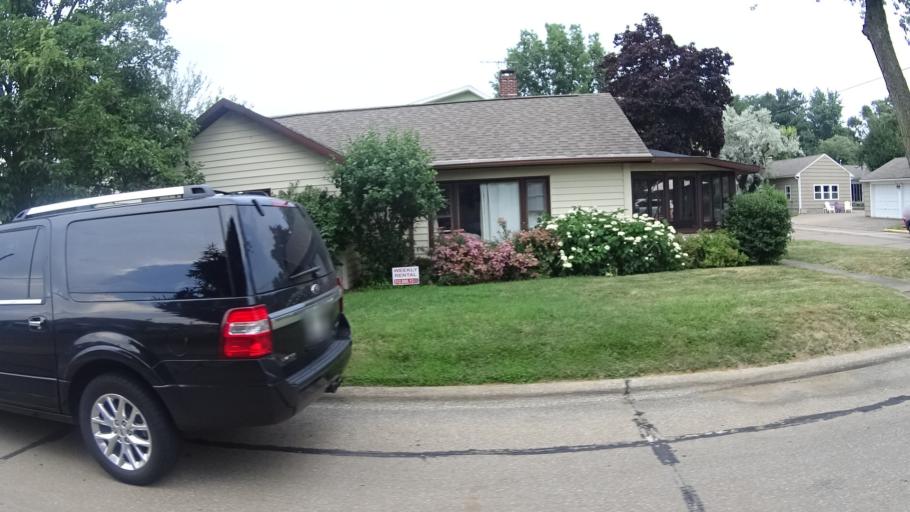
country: US
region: Ohio
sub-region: Erie County
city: Huron
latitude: 41.3918
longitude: -82.5404
